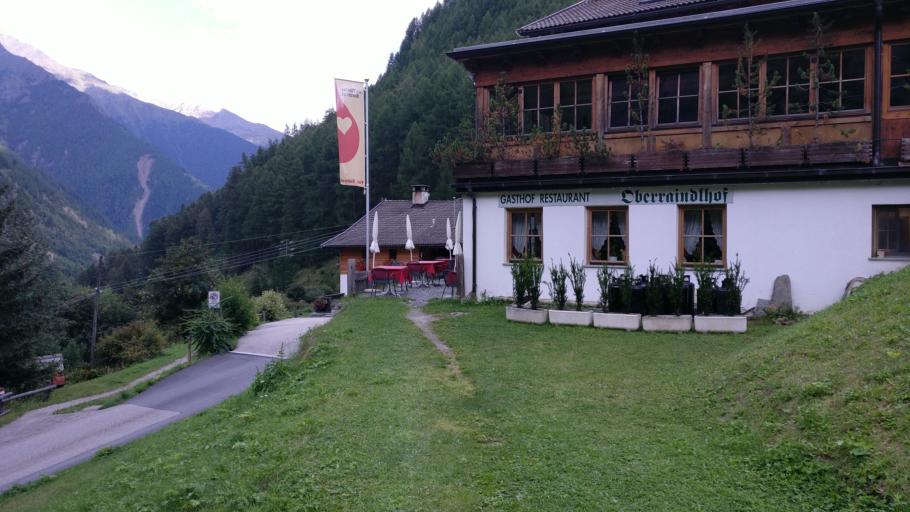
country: IT
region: Trentino-Alto Adige
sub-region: Bolzano
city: Senales
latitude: 46.7140
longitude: 10.8828
